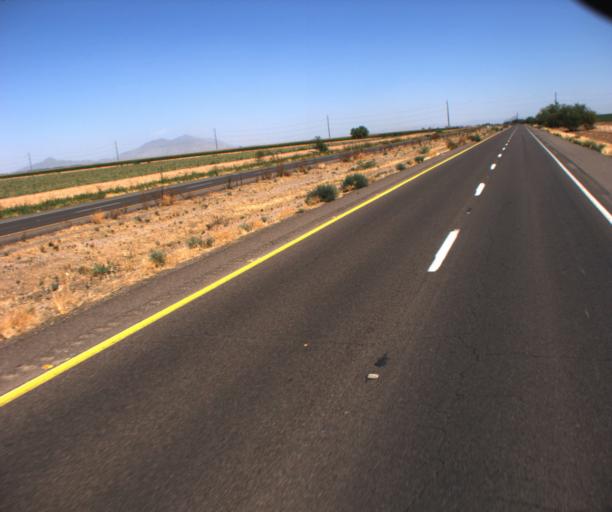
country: US
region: Arizona
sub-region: Pinal County
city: Maricopa
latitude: 32.9530
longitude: -112.0479
